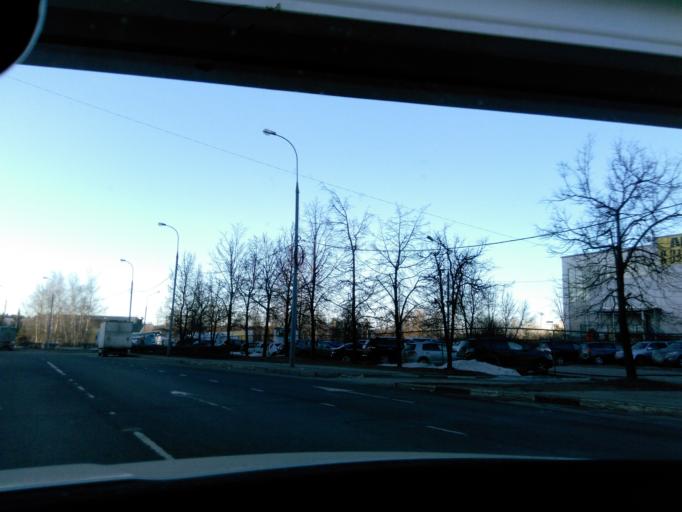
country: RU
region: Moskovskaya
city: Rzhavki
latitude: 55.9904
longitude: 37.2239
